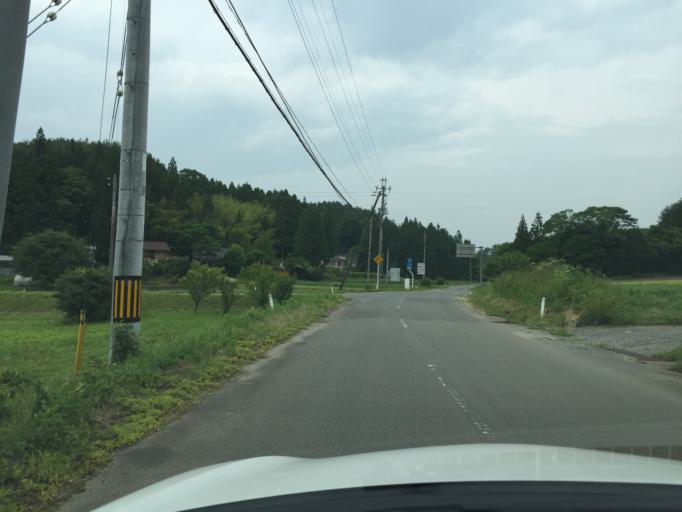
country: JP
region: Fukushima
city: Iwaki
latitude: 37.2000
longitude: 140.7212
